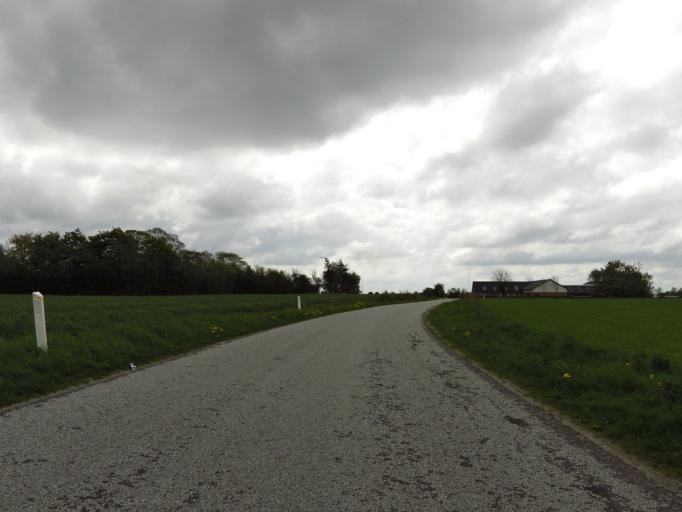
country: DK
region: South Denmark
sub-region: Haderslev Kommune
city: Gram
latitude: 55.2304
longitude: 8.9897
